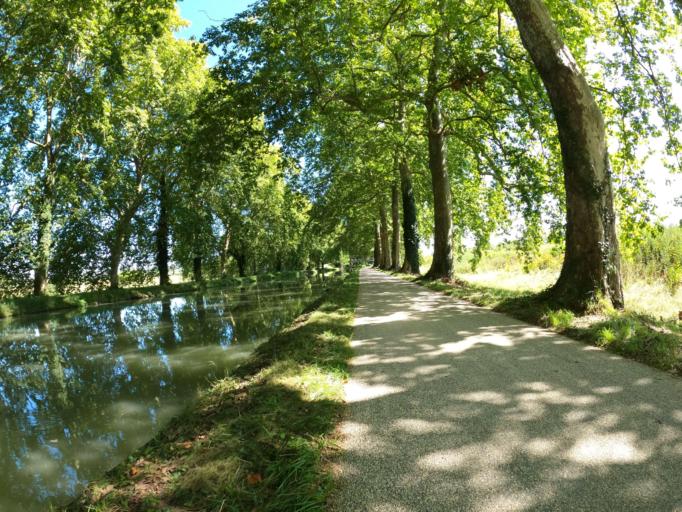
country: FR
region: Midi-Pyrenees
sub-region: Departement du Tarn-et-Garonne
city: Auvillar
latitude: 44.0941
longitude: 0.9481
